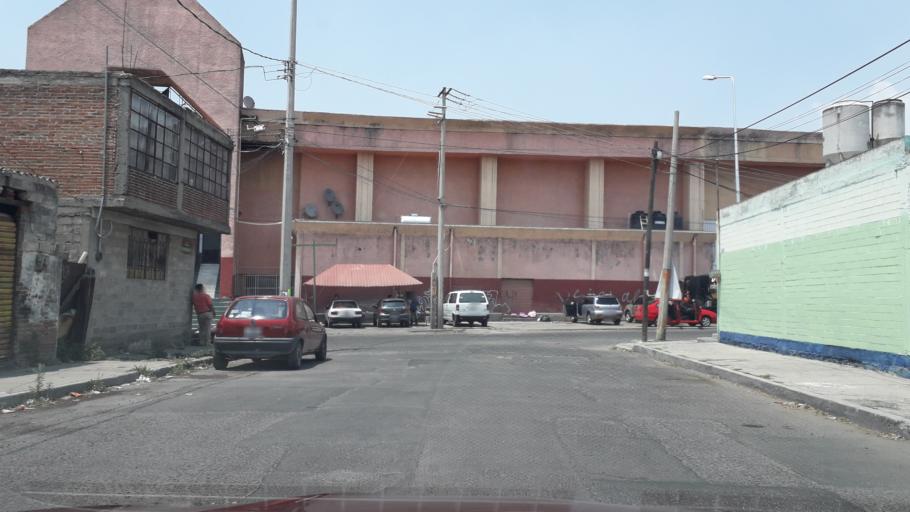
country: MX
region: Puebla
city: Puebla
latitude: 19.0481
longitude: -98.1663
